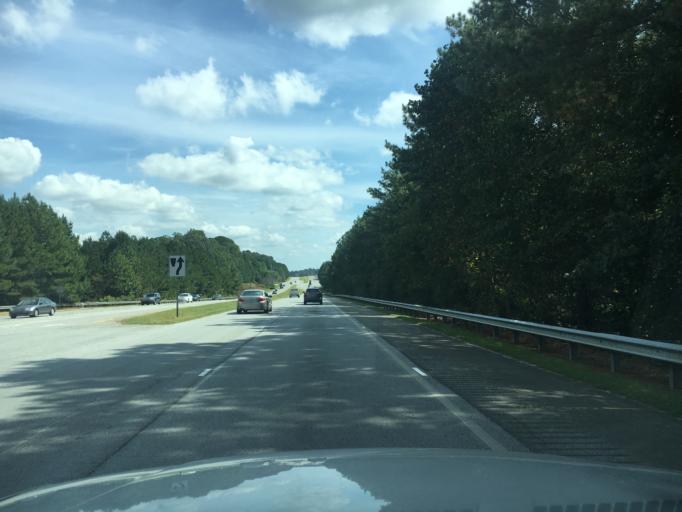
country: US
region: Georgia
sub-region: Gwinnett County
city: Duluth
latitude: 34.0223
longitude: -84.1345
